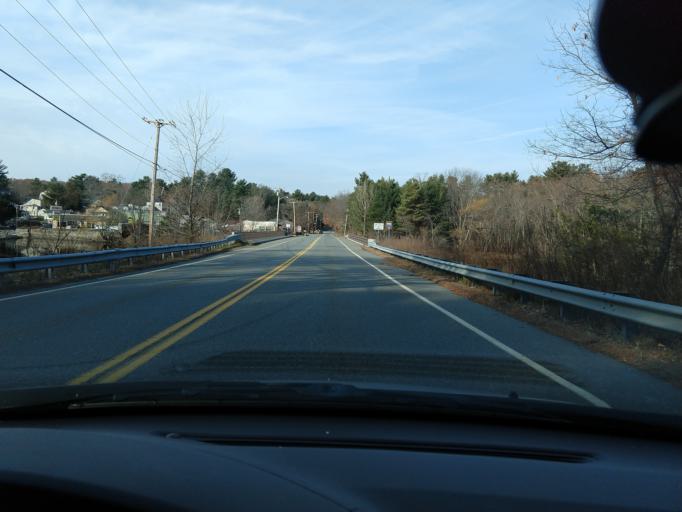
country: US
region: Massachusetts
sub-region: Middlesex County
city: Billerica
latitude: 42.5345
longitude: -71.2988
